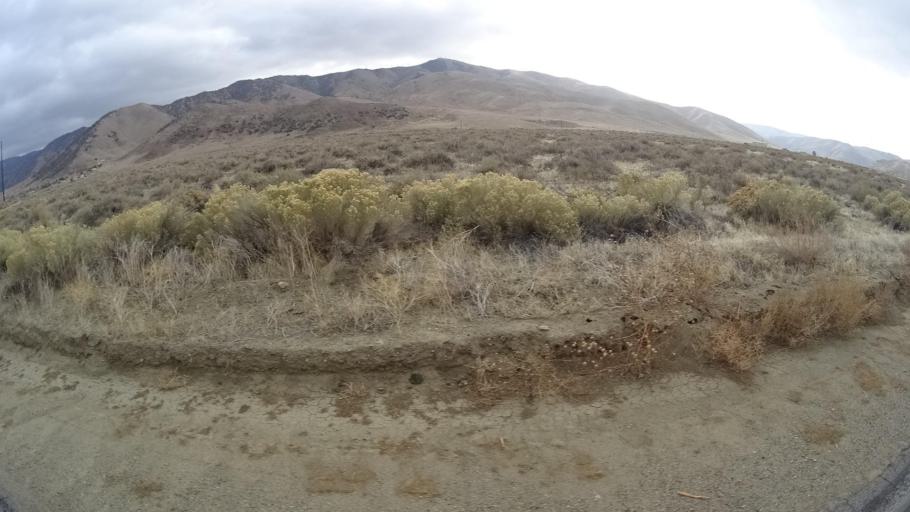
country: US
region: California
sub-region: Kern County
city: Tehachapi
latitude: 35.1367
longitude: -118.3246
